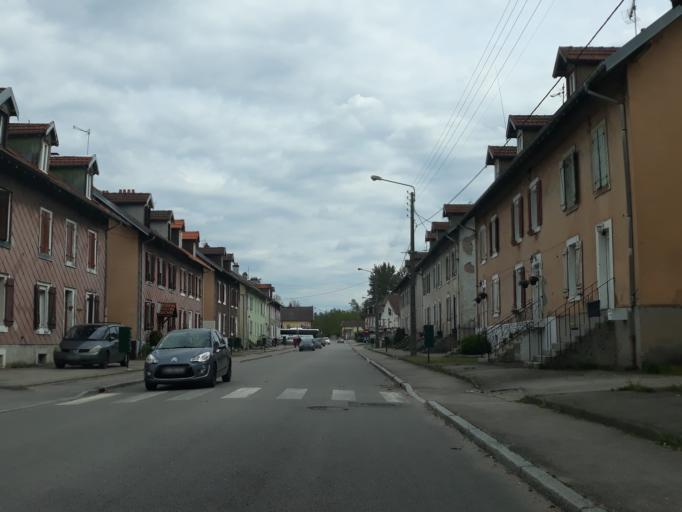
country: FR
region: Lorraine
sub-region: Departement des Vosges
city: Bruyeres
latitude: 48.1810
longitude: 6.7553
